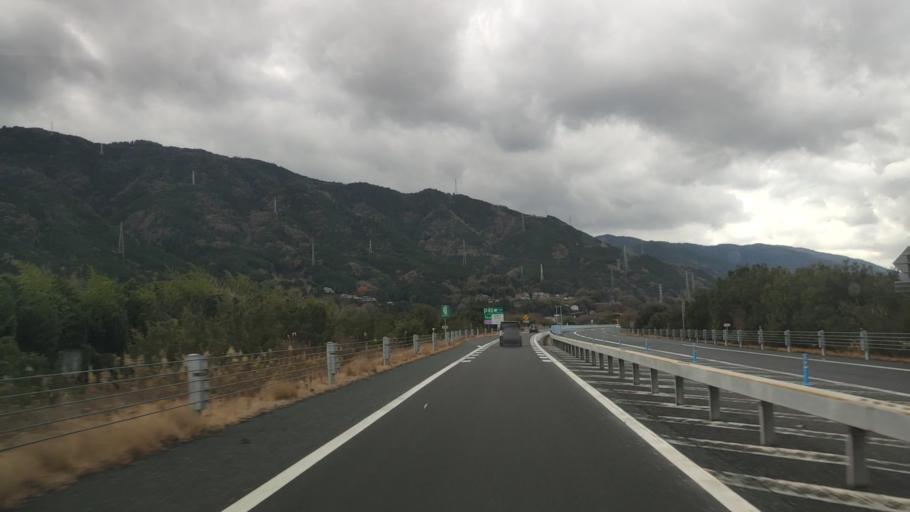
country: JP
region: Tokushima
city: Ikedacho
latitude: 34.0389
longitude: 133.9069
